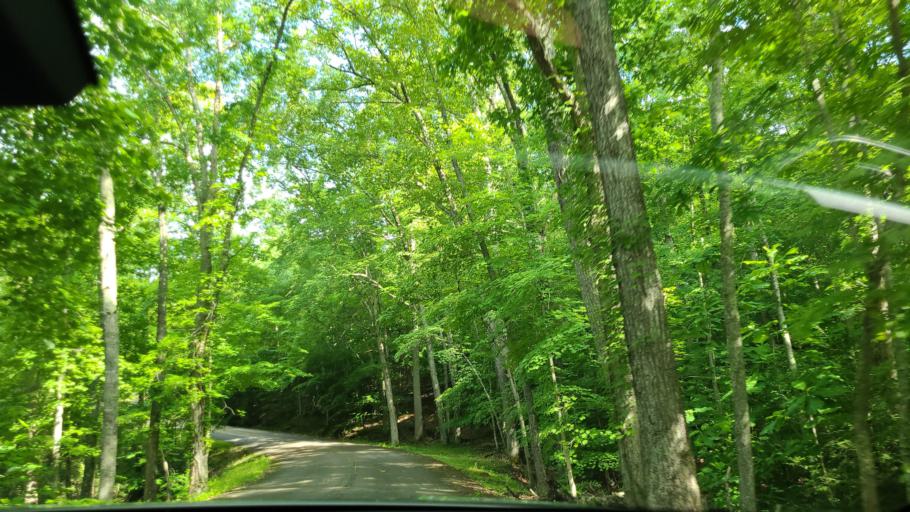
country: US
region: Kentucky
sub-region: Bell County
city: Pineville
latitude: 36.7416
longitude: -83.7127
